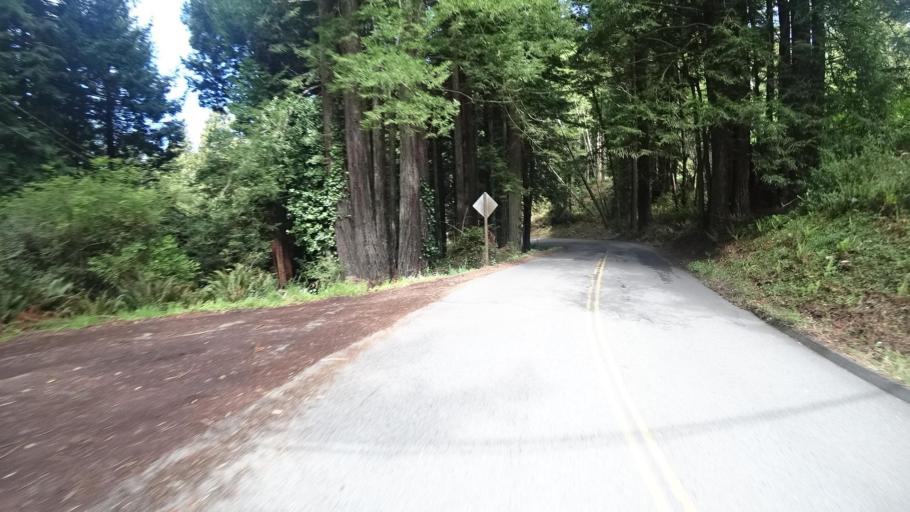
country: US
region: California
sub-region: Humboldt County
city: Arcata
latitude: 40.8699
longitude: -124.0617
